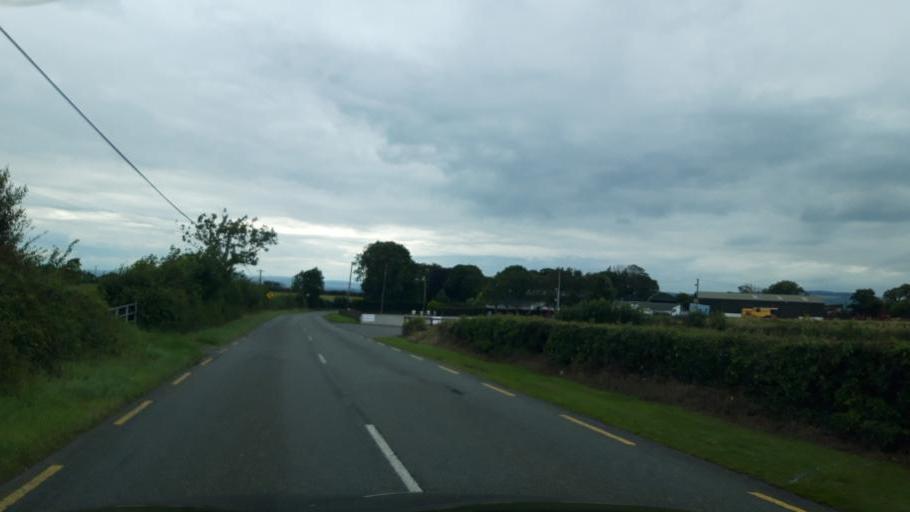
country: IE
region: Leinster
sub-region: Kilkenny
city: Ballyragget
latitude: 52.7980
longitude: -7.3086
